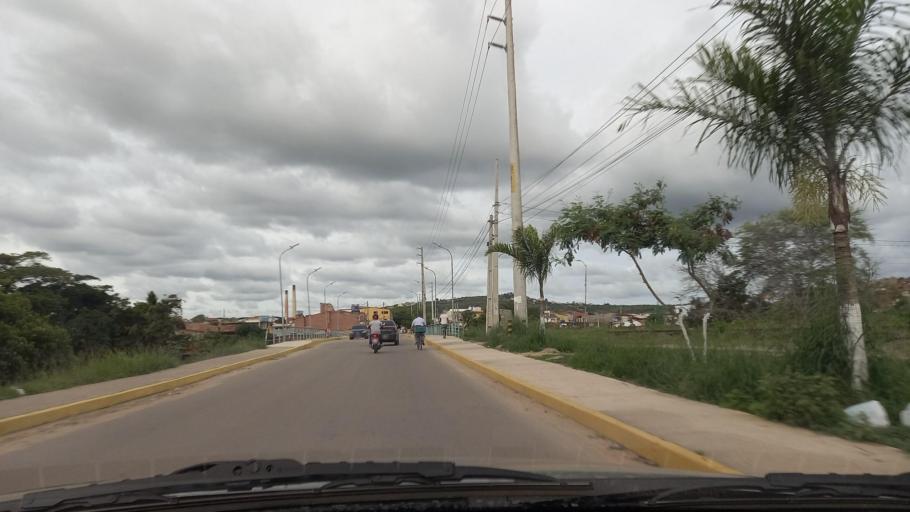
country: BR
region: Pernambuco
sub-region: Gravata
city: Gravata
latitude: -8.2051
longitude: -35.5659
